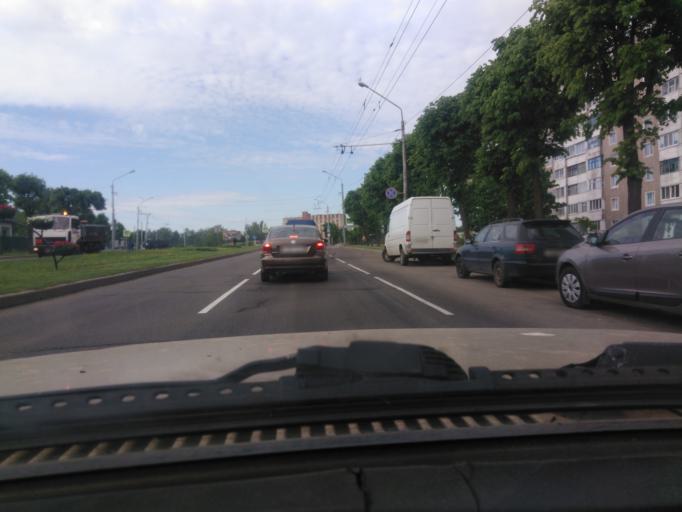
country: BY
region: Mogilev
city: Mahilyow
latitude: 53.9001
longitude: 30.2968
